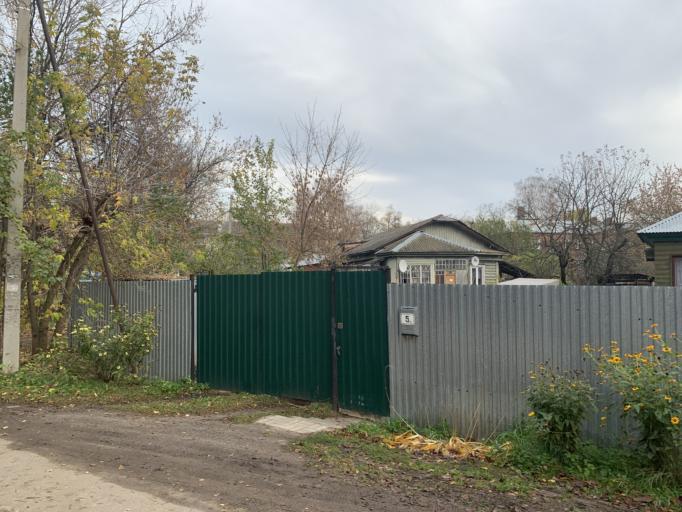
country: RU
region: Moskovskaya
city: Lesnyye Polyany
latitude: 55.9887
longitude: 37.8502
